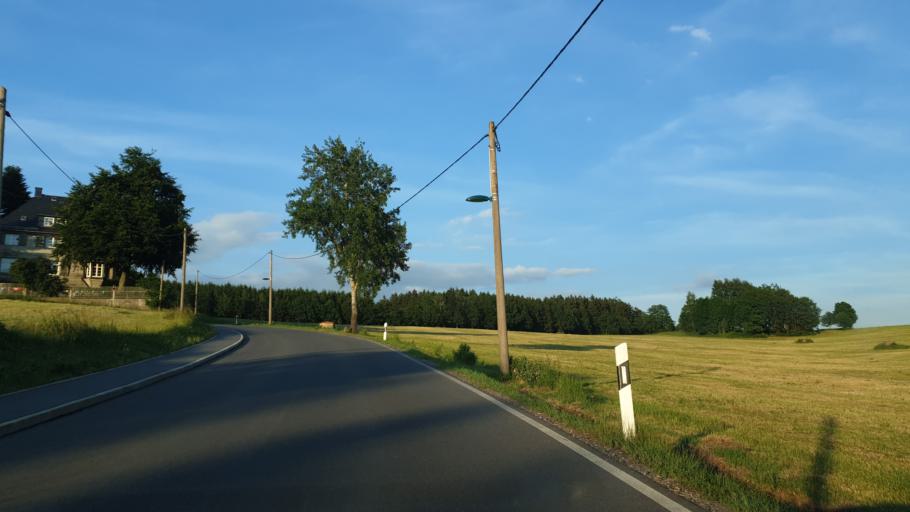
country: DE
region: Saxony
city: Lossnitz
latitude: 50.6627
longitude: 12.7255
